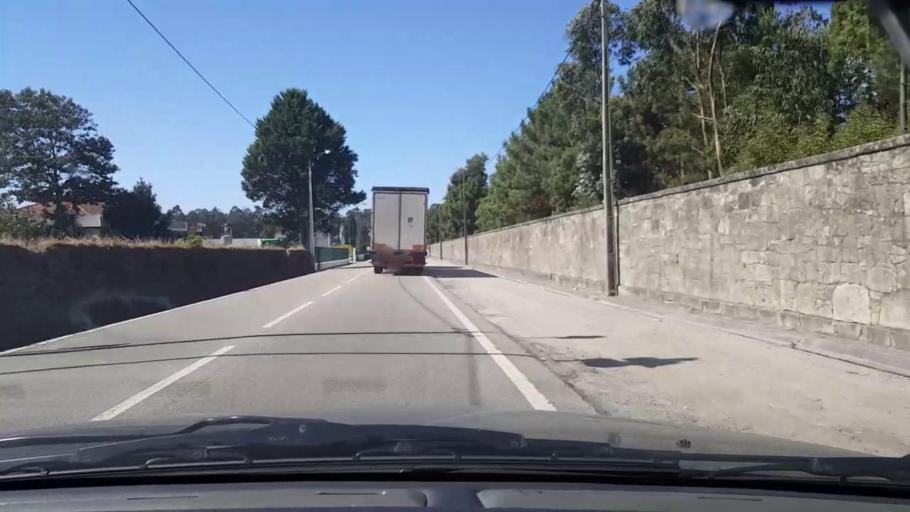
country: PT
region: Porto
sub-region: Vila do Conde
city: Arvore
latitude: 41.3381
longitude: -8.6869
